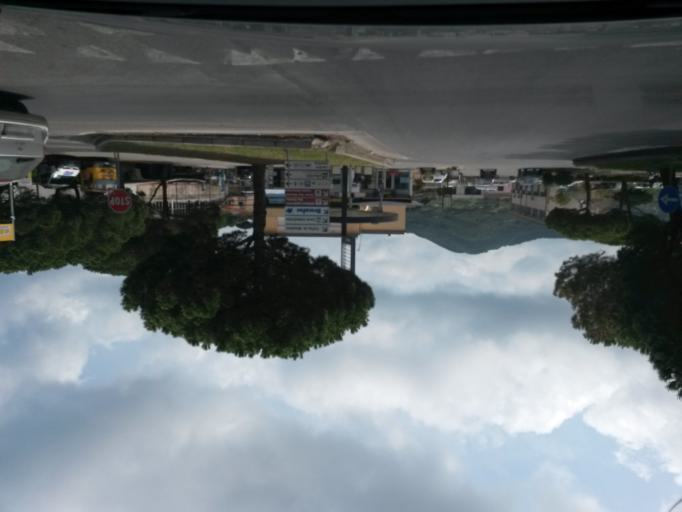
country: IT
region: Tuscany
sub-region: Provincia di Livorno
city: Portoferraio
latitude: 42.8113
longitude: 10.3150
